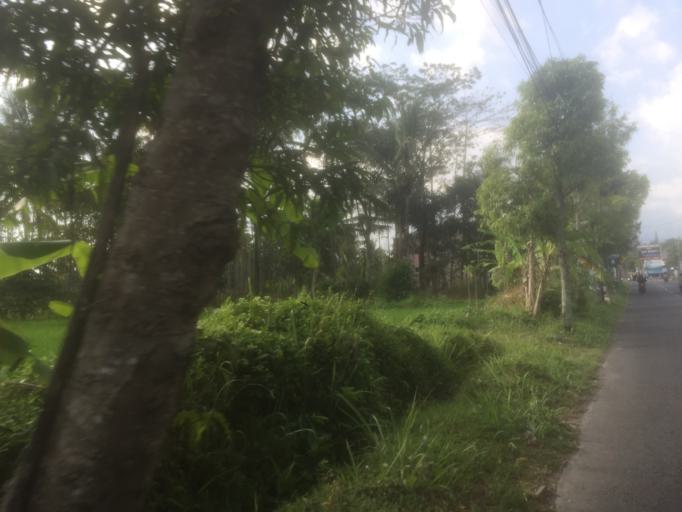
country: ID
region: Daerah Istimewa Yogyakarta
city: Sleman
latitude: -7.6482
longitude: 110.4240
